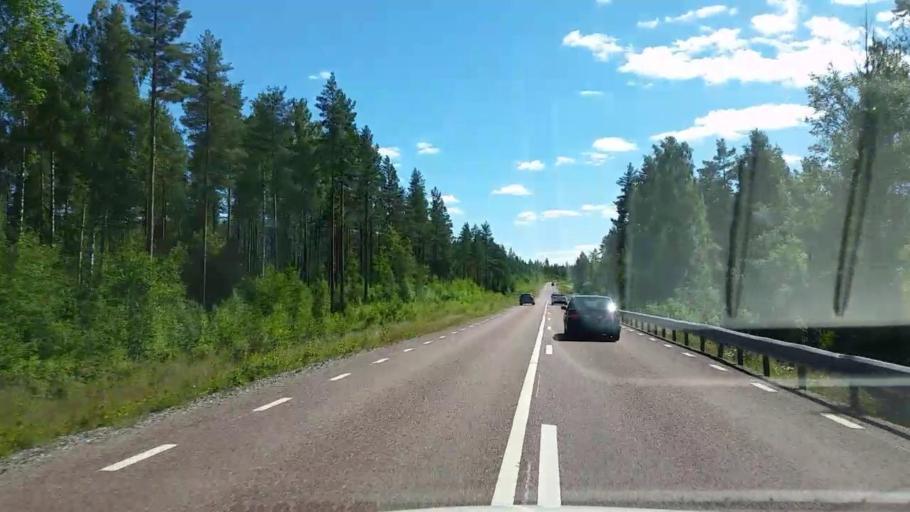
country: SE
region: Gaevleborg
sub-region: Ovanakers Kommun
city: Edsbyn
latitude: 61.2234
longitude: 15.8765
